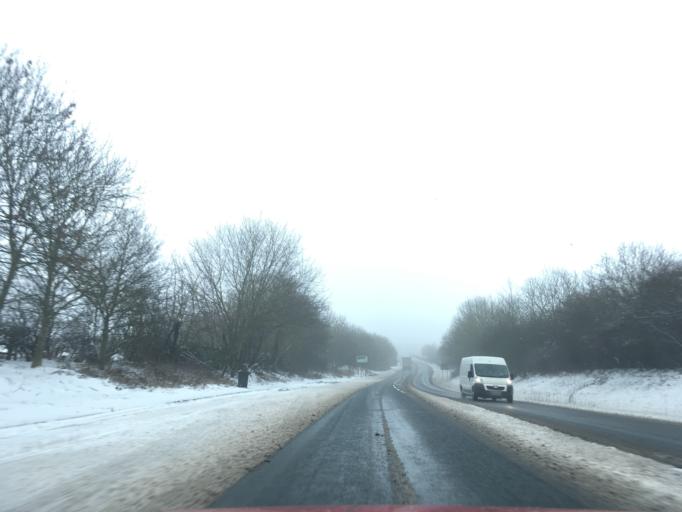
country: GB
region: England
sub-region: Warwickshire
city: Stratford-upon-Avon
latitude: 52.2388
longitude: -1.6602
